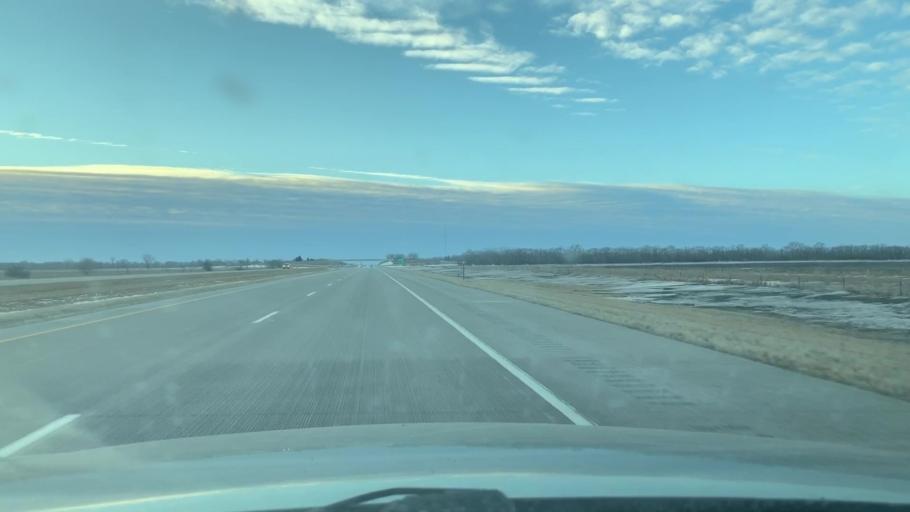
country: US
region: North Dakota
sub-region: Cass County
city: Casselton
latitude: 46.8749
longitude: -97.4198
